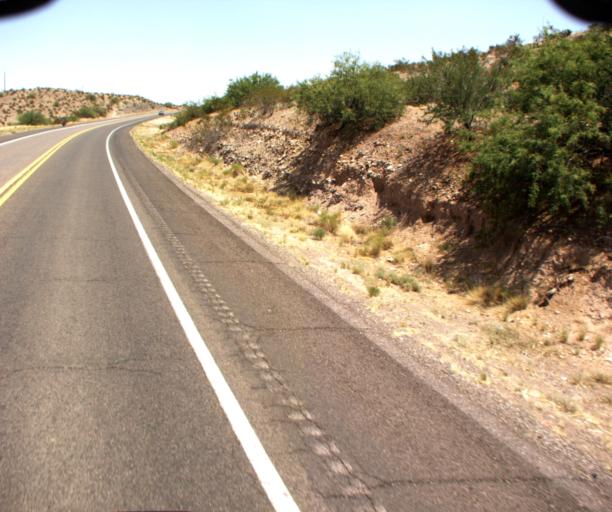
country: US
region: Arizona
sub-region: Graham County
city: Safford
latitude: 32.8127
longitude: -109.5931
